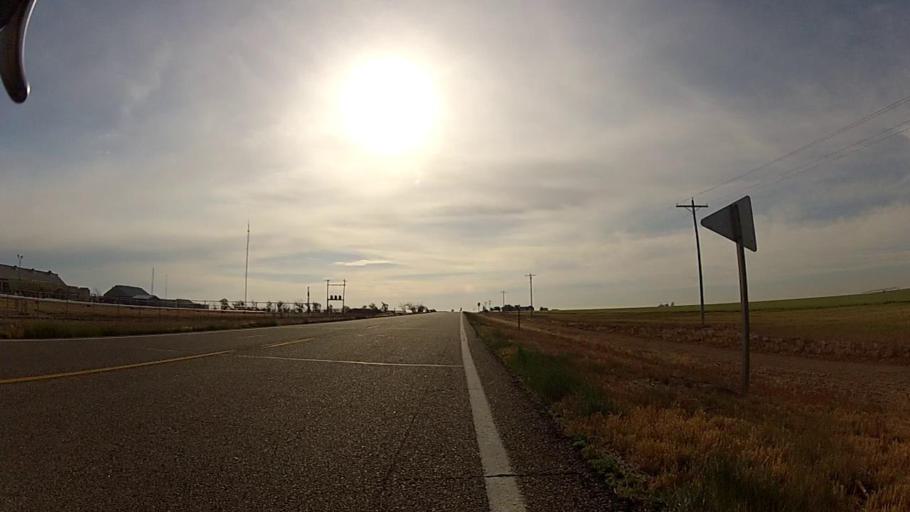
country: US
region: Kansas
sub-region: Grant County
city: Ulysses
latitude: 37.5765
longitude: -101.4885
